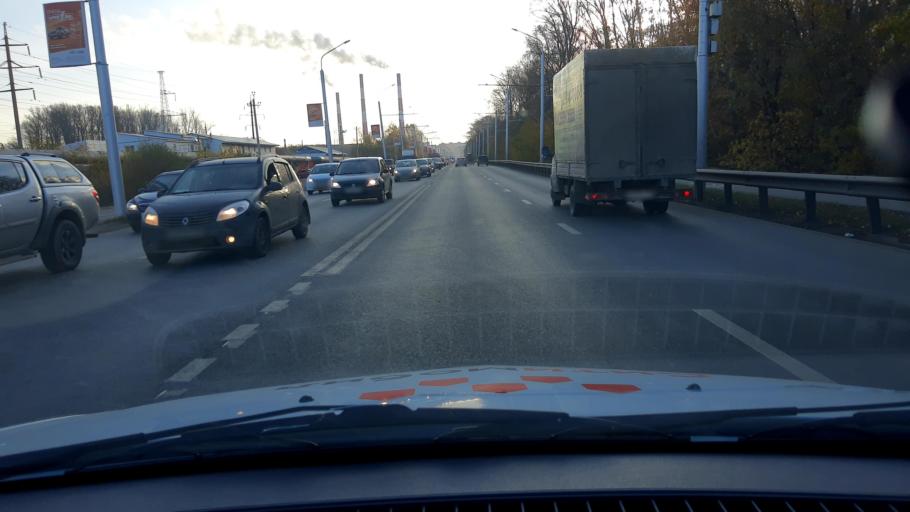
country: RU
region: Bashkortostan
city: Ufa
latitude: 54.7911
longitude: 56.0947
